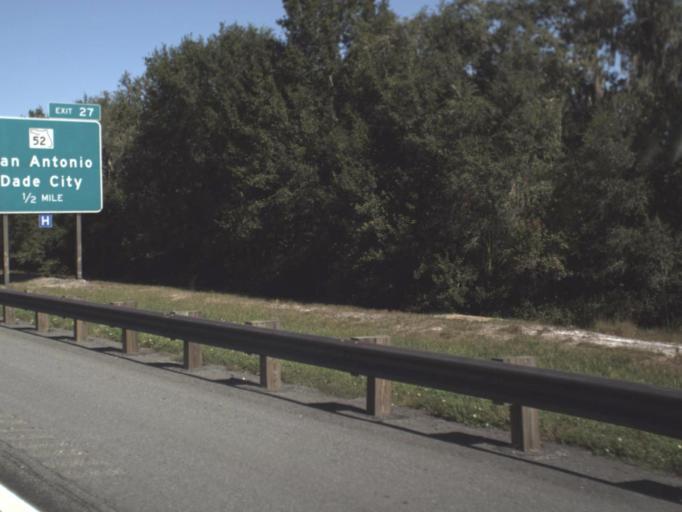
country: US
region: Florida
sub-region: Pasco County
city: Shady Hills
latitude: 28.3178
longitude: -82.5518
